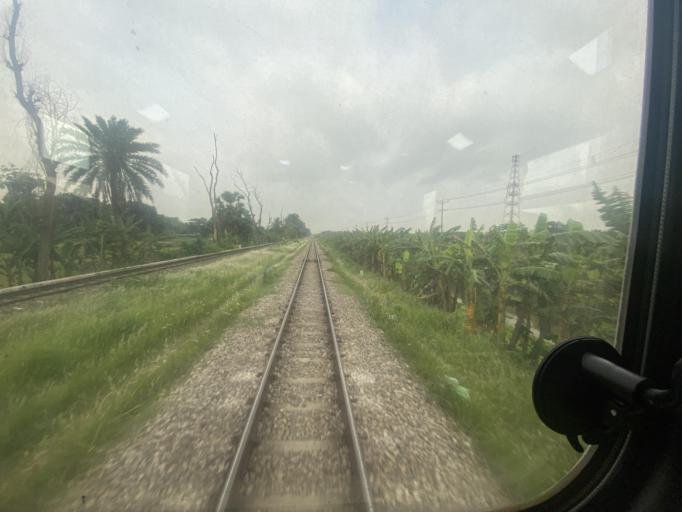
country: BD
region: Dhaka
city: Tungi
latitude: 23.9325
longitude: 90.5181
